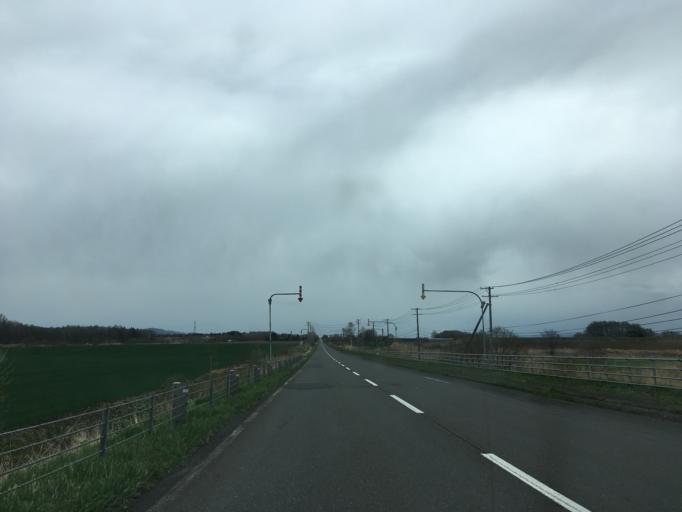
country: JP
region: Hokkaido
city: Chitose
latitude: 42.9045
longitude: 141.8127
